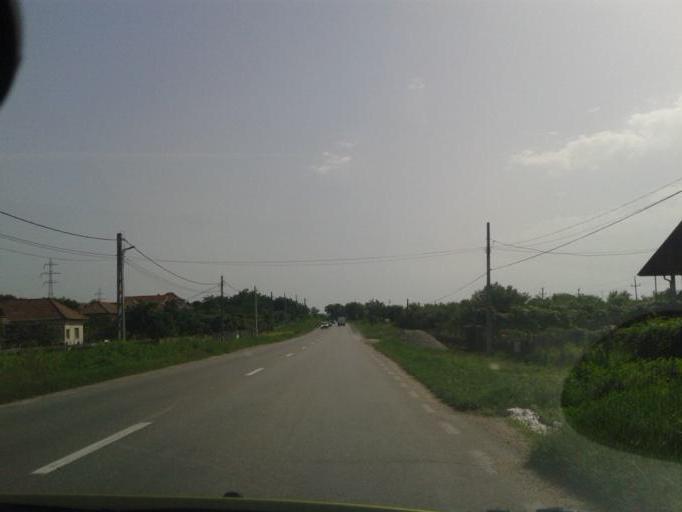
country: RO
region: Valcea
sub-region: Comuna Mihaesti
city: Mihaesti
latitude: 45.0433
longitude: 24.2660
